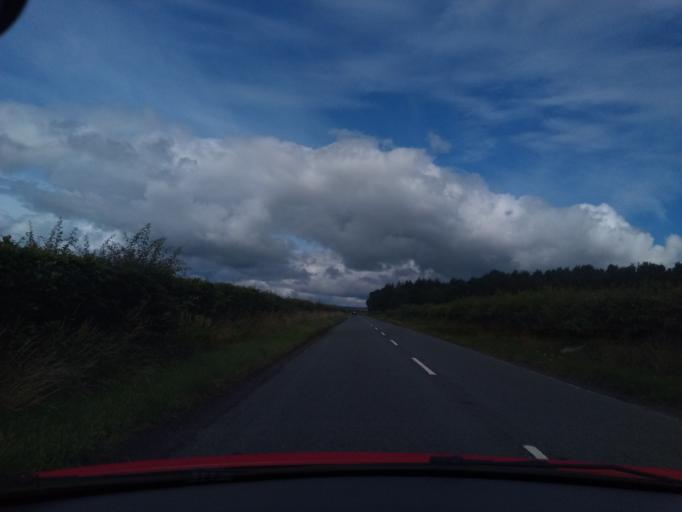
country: GB
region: Scotland
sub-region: The Scottish Borders
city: Lauder
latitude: 55.7327
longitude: -2.7351
